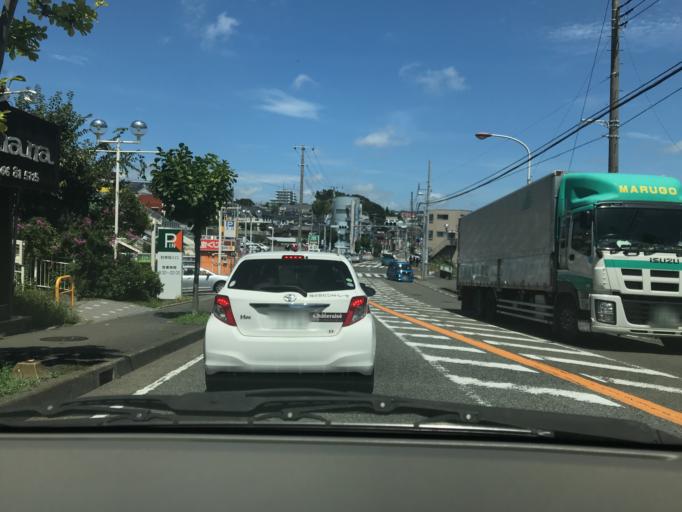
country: JP
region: Kanagawa
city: Fujisawa
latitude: 35.3606
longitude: 139.4679
